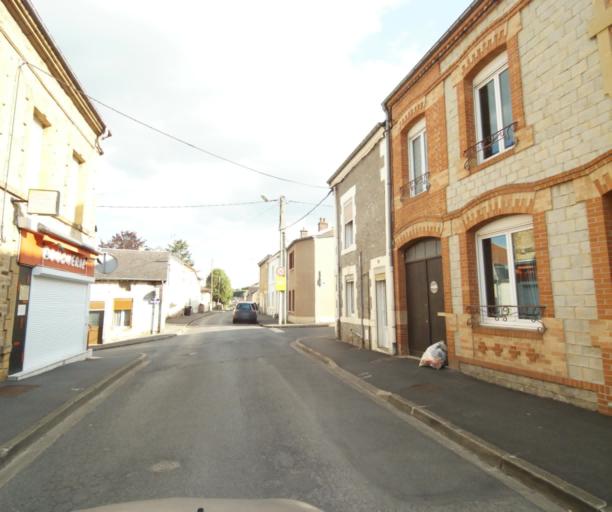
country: FR
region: Champagne-Ardenne
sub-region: Departement des Ardennes
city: Montcy-Notre-Dame
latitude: 49.7769
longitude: 4.7343
